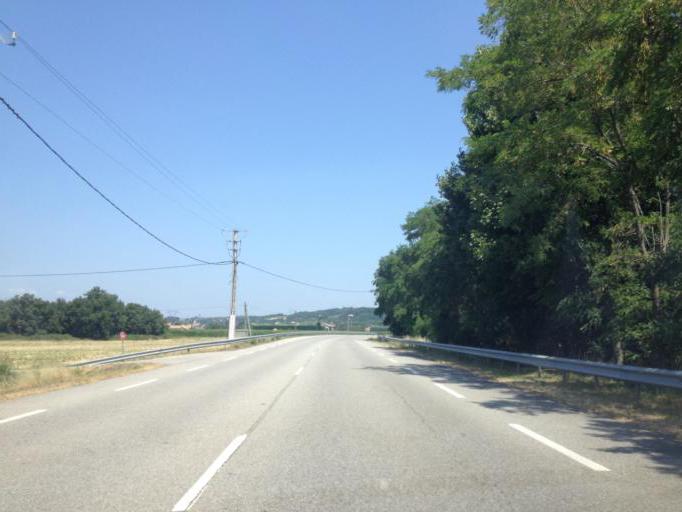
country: FR
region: Rhone-Alpes
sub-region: Departement de la Drome
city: Beaumont-Monteux
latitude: 45.0389
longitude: 4.9310
